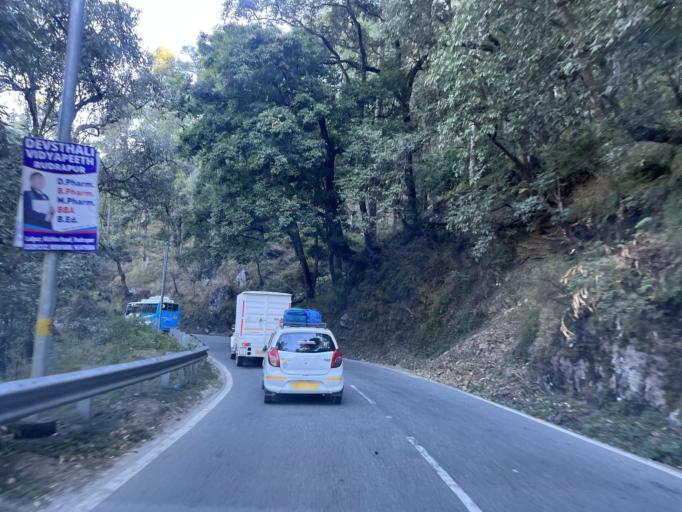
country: IN
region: Uttarakhand
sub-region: Naini Tal
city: Bhowali
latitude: 29.3954
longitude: 79.5115
